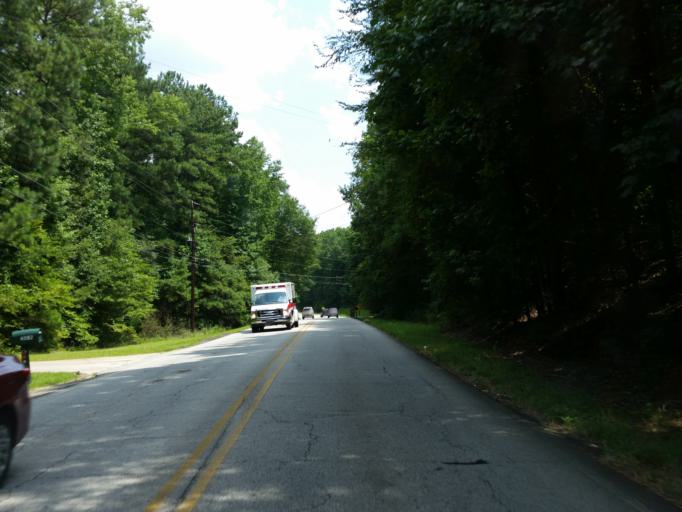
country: US
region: Georgia
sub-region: Henry County
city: Stockbridge
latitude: 33.5018
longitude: -84.2614
